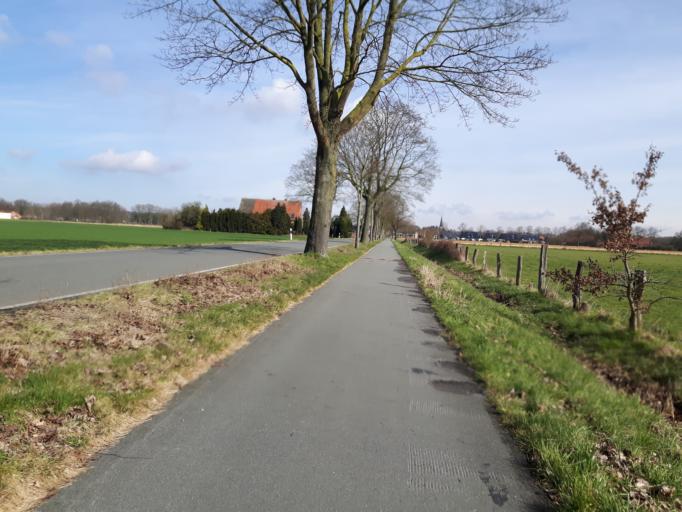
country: DE
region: North Rhine-Westphalia
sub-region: Regierungsbezirk Munster
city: Dulmen
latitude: 51.8137
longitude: 7.2704
